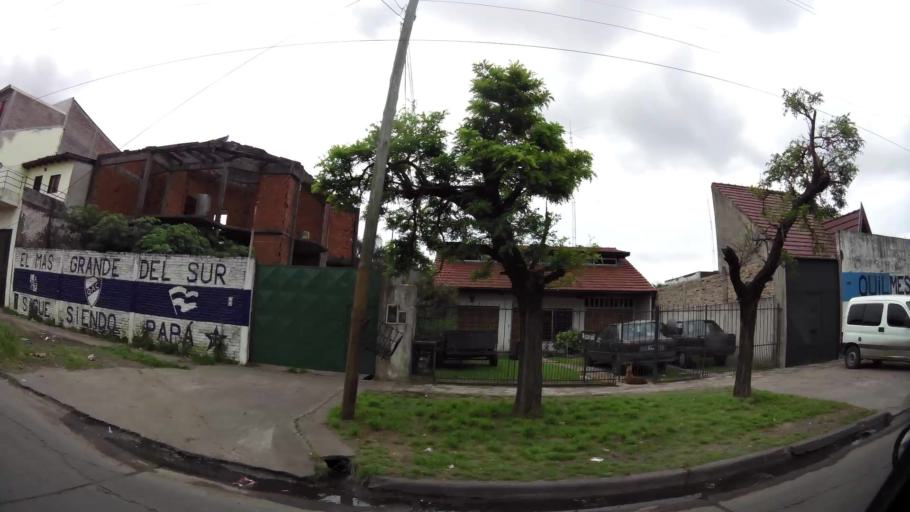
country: AR
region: Buenos Aires
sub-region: Partido de Quilmes
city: Quilmes
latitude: -34.7679
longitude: -58.2803
